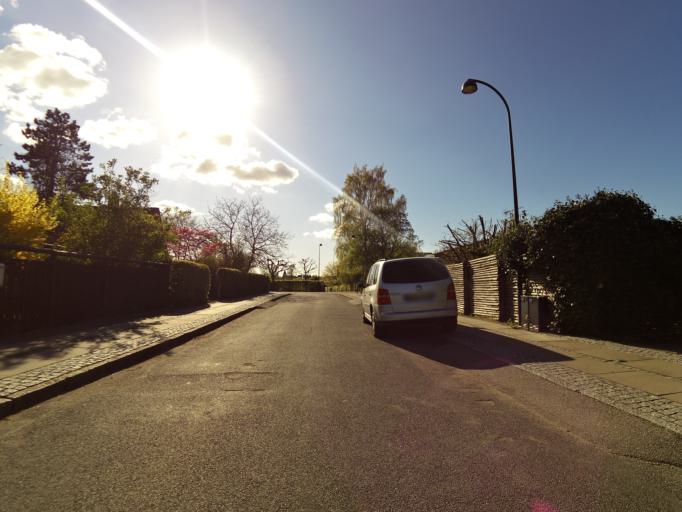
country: DK
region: Capital Region
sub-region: Lyngby-Tarbaek Kommune
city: Kongens Lyngby
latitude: 55.7356
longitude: 12.5250
